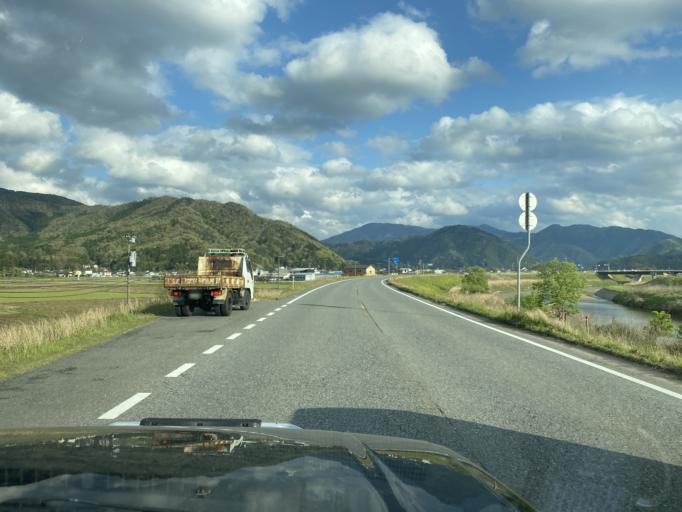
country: JP
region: Hyogo
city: Toyooka
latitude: 35.4844
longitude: 134.8604
